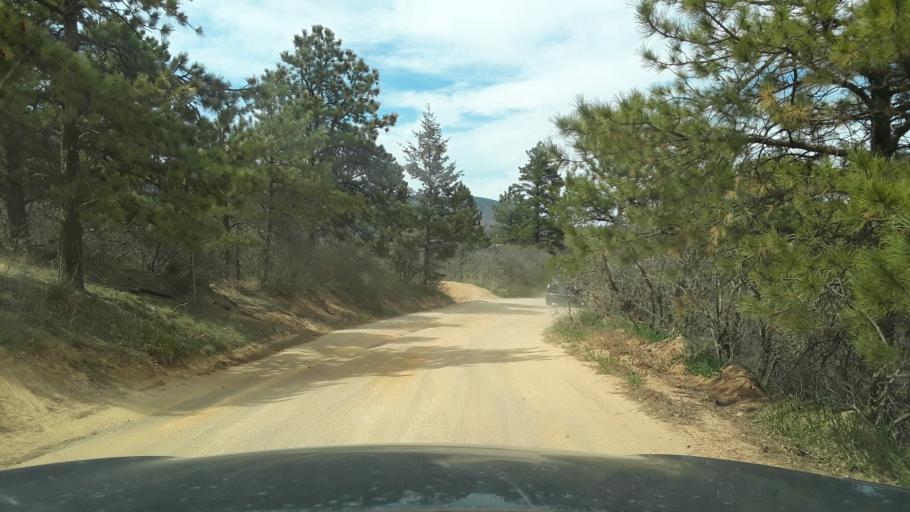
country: US
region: Colorado
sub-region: El Paso County
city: Palmer Lake
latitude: 39.0878
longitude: -104.9113
